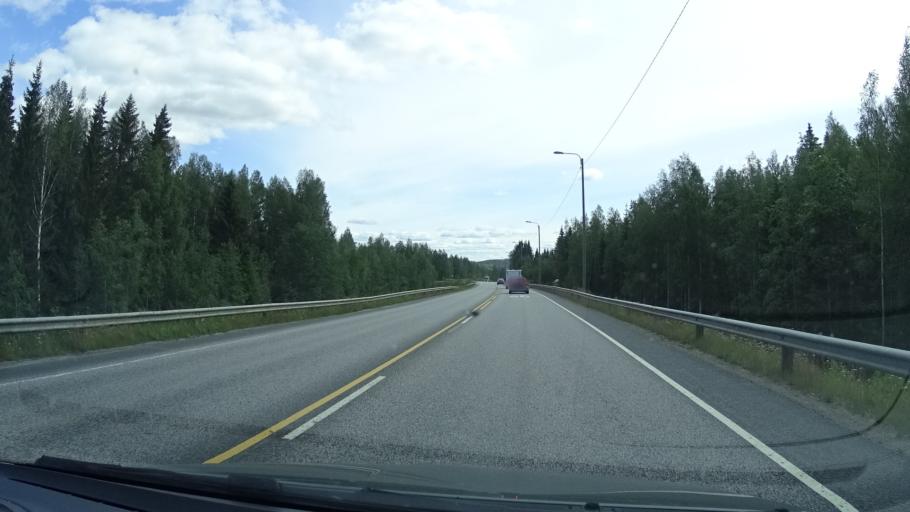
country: FI
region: Central Finland
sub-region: Jyvaeskylae
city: Jyvaeskylae
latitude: 62.2610
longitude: 25.5954
